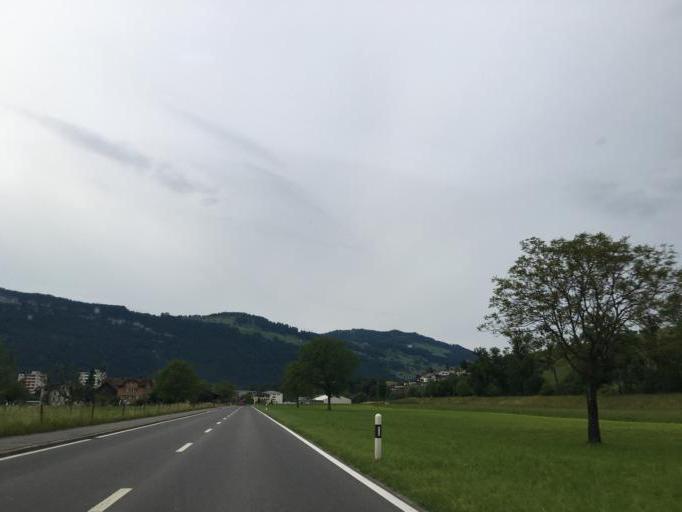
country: CH
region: Nidwalden
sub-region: Nidwalden
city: Stans
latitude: 46.9508
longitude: 8.3877
